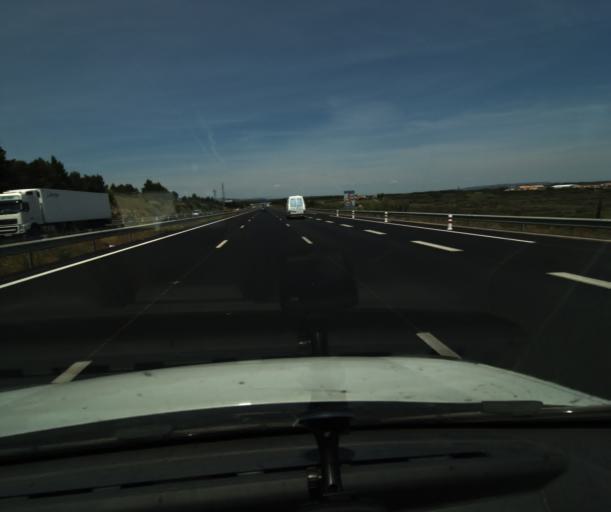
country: FR
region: Languedoc-Roussillon
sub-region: Departement de l'Aude
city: Sigean
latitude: 43.0245
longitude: 2.9525
